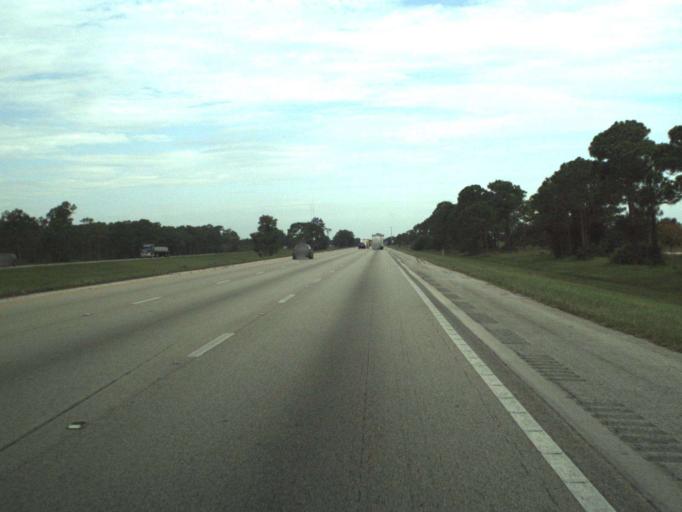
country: US
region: Florida
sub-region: Martin County
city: Palm City
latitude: 27.1273
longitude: -80.2953
